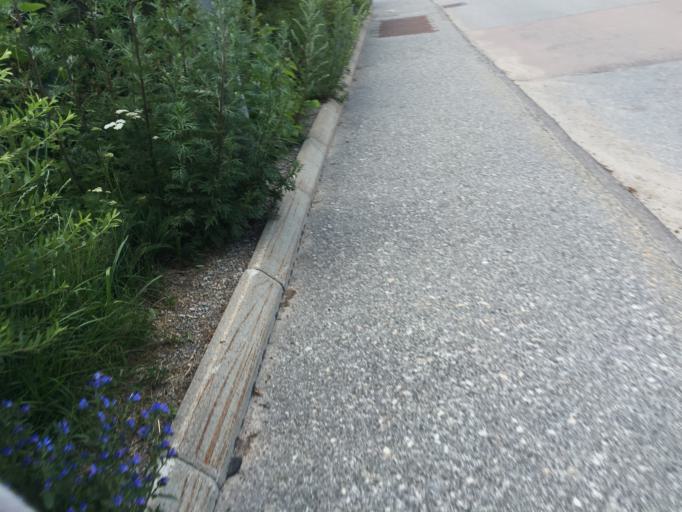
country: SE
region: Stockholm
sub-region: Lidingo
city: Brevik
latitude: 59.3168
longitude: 18.2331
